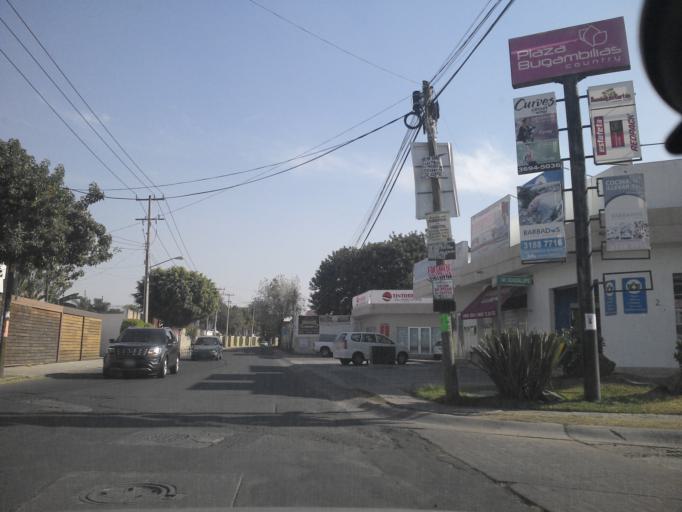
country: MX
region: Jalisco
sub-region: Tlajomulco de Zuniga
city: Palomar
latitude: 20.6128
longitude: -103.4540
